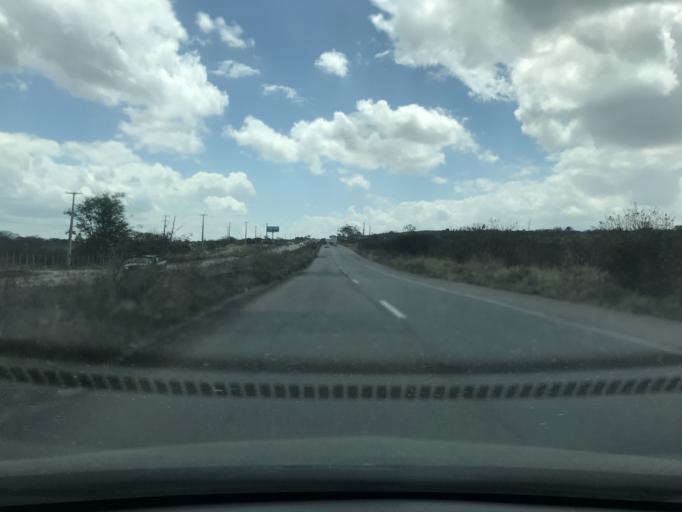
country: BR
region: Pernambuco
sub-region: Caruaru
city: Caruaru
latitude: -8.3026
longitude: -35.9209
